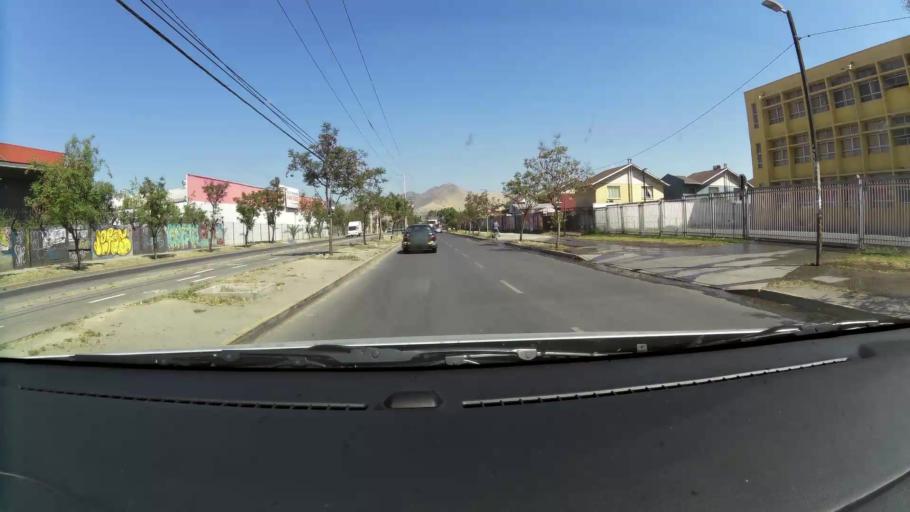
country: CL
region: Santiago Metropolitan
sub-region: Provincia de Maipo
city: San Bernardo
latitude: -33.6121
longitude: -70.6938
